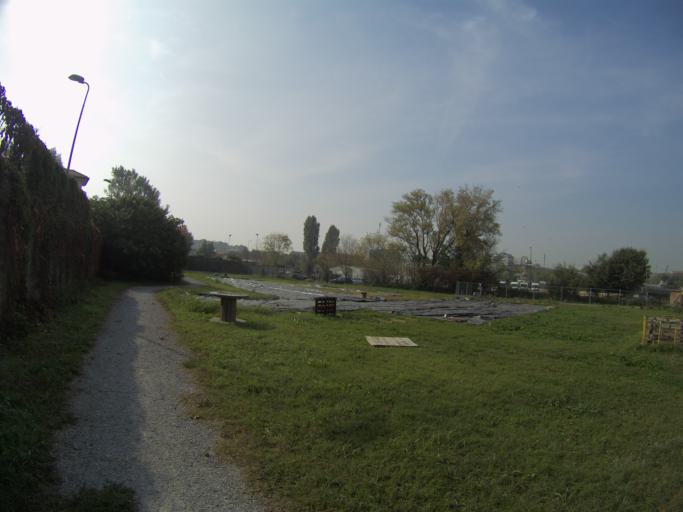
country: IT
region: Lombardy
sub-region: Citta metropolitana di Milano
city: Linate
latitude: 45.4654
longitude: 9.2413
